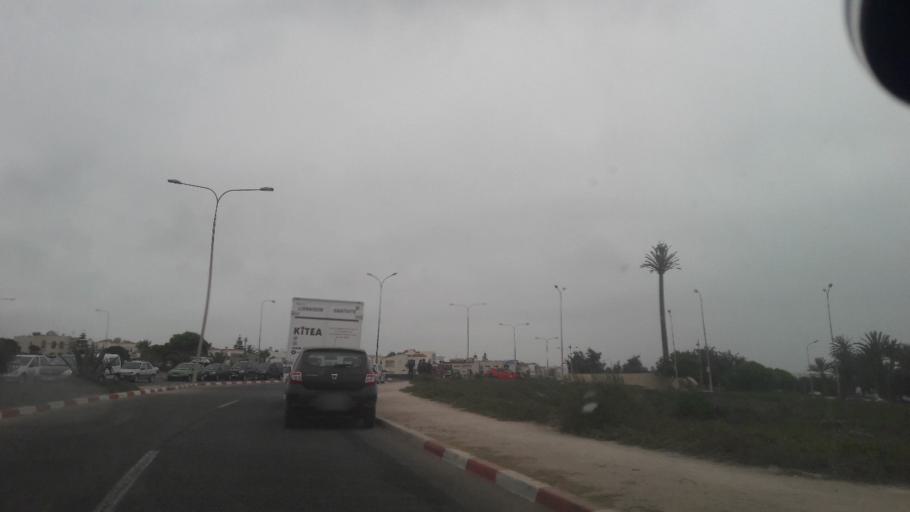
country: MA
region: Souss-Massa-Draa
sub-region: Agadir-Ida-ou-Tnan
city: Agadir
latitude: 30.3965
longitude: -9.5953
